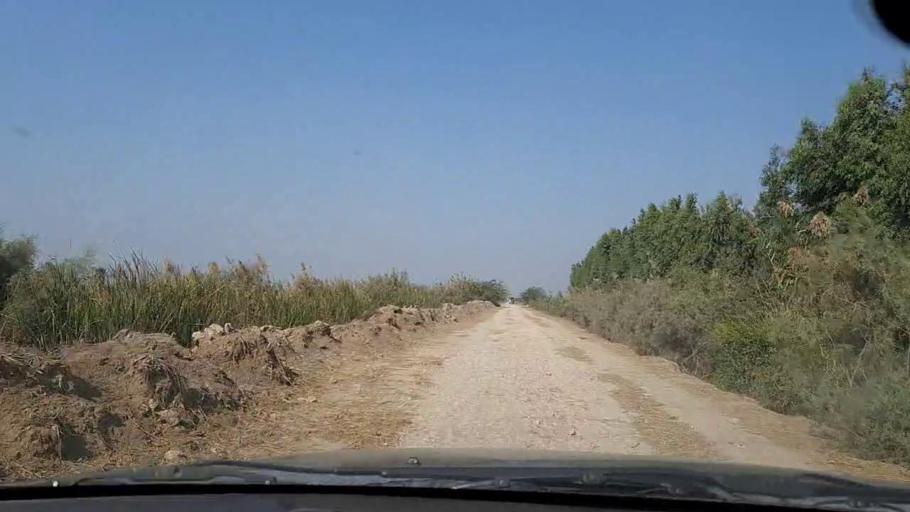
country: PK
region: Sindh
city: Mirpur Sakro
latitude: 24.3510
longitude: 67.6831
